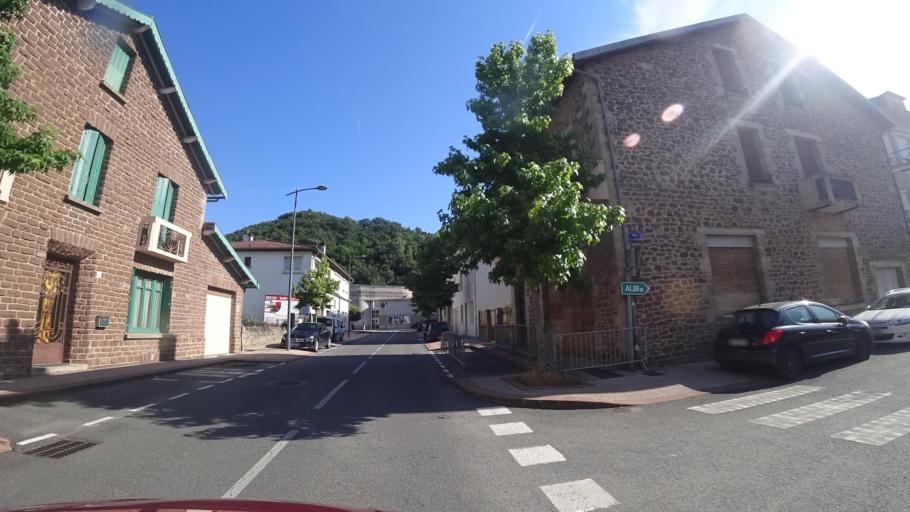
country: FR
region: Midi-Pyrenees
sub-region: Departement de l'Aveyron
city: Saint-Affrique
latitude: 43.9565
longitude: 2.8841
